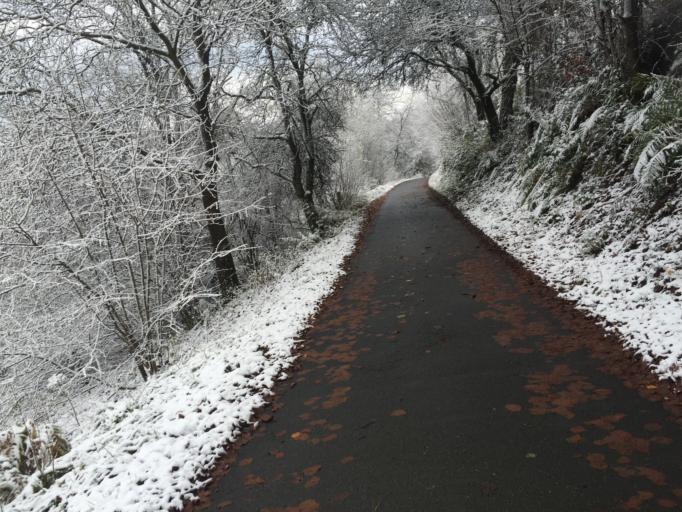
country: DE
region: Hesse
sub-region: Regierungsbezirk Darmstadt
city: Wald-Michelbach
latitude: 49.5561
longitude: 8.8858
